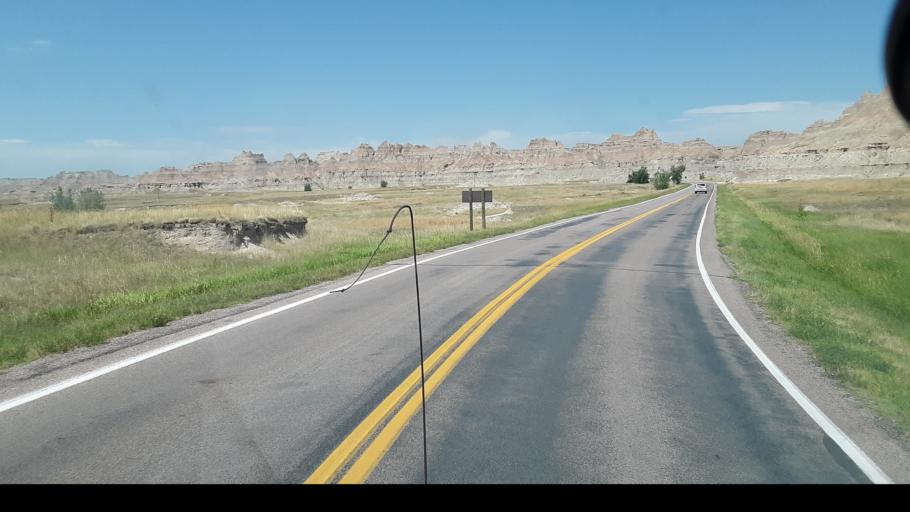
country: US
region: South Dakota
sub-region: Haakon County
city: Philip
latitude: 43.7480
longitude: -101.9496
